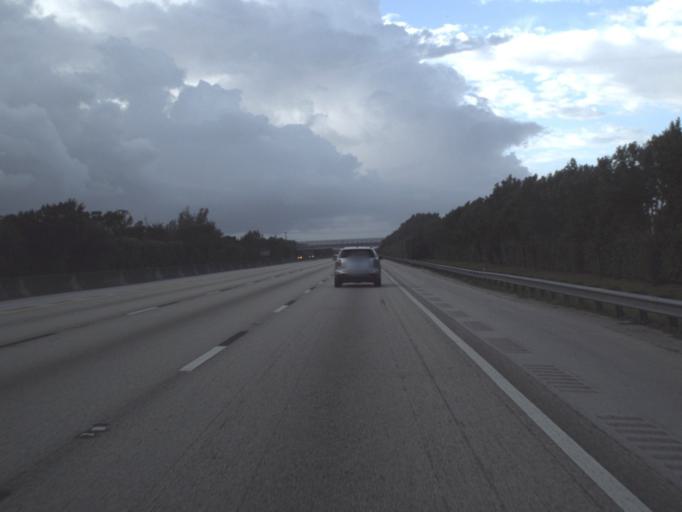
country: US
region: Florida
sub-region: Palm Beach County
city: Boca Pointe
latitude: 26.3555
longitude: -80.1708
